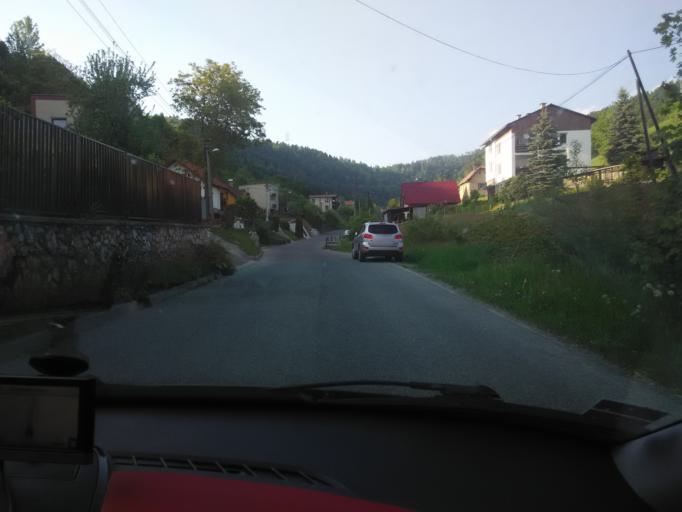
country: SK
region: Presovsky
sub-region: Okres Presov
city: Levoca
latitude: 49.0342
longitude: 20.6004
